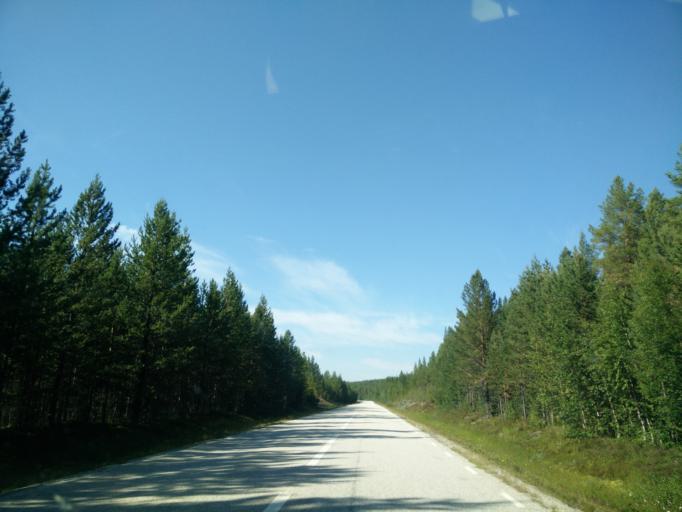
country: SE
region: Jaemtland
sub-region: Are Kommun
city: Jarpen
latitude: 62.8184
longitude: 13.5090
